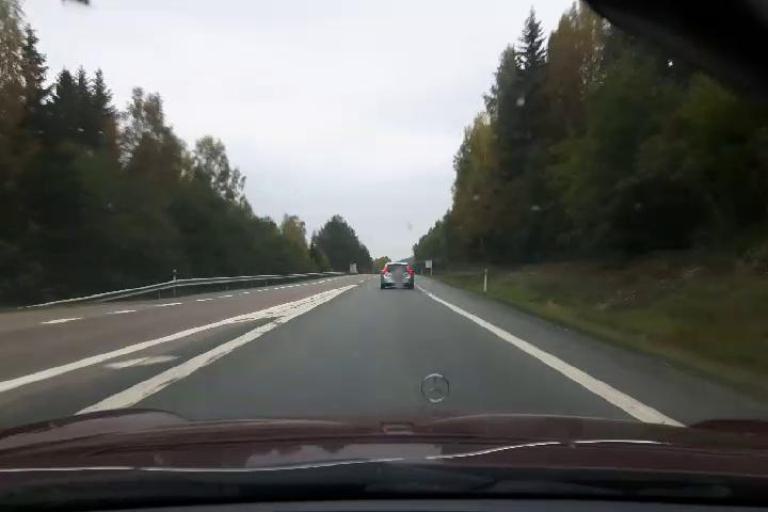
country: SE
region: Vaesternorrland
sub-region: Kramfors Kommun
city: Nordingra
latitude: 63.0393
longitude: 18.3265
